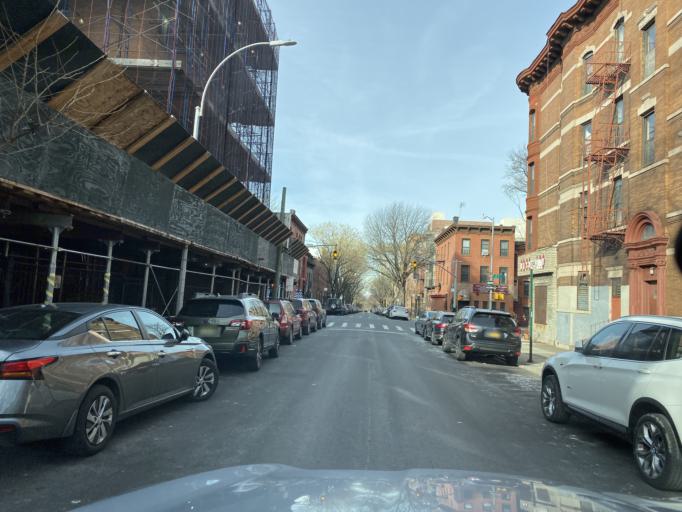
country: US
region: New York
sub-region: Kings County
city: Brooklyn
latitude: 40.6631
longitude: -73.9806
